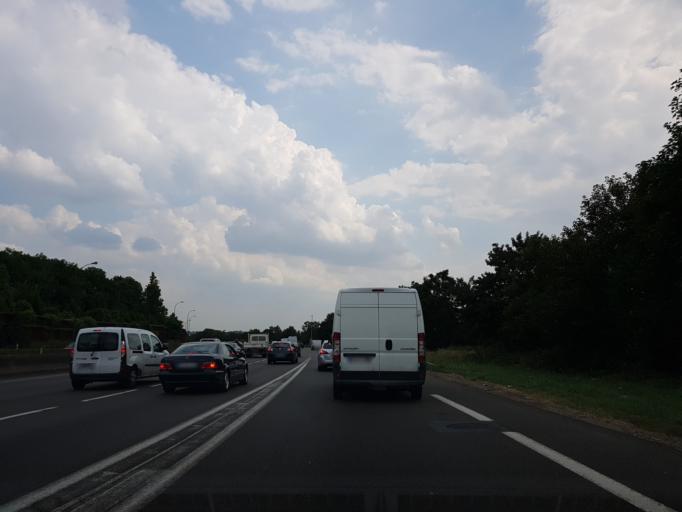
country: FR
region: Ile-de-France
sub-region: Departement de l'Essonne
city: Longjumeau
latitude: 48.7062
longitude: 2.3058
